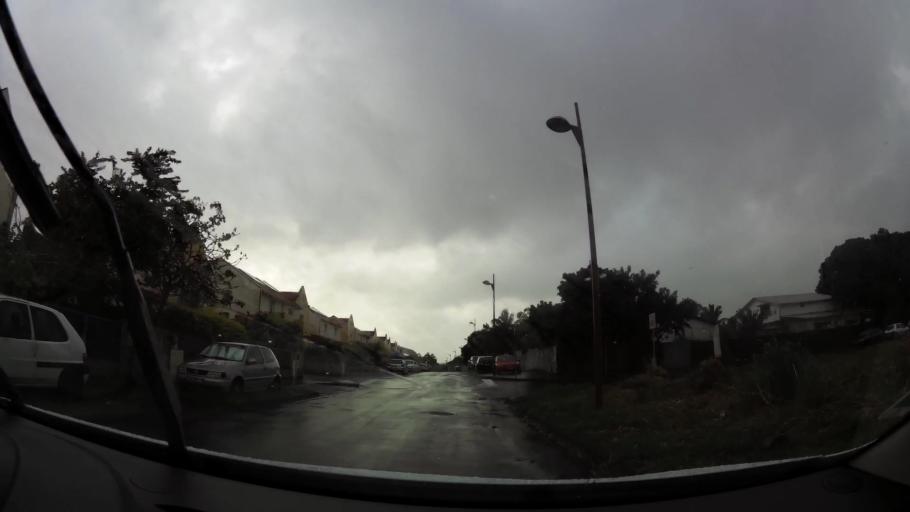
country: RE
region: Reunion
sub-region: Reunion
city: Saint-Andre
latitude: -20.9750
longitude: 55.6575
